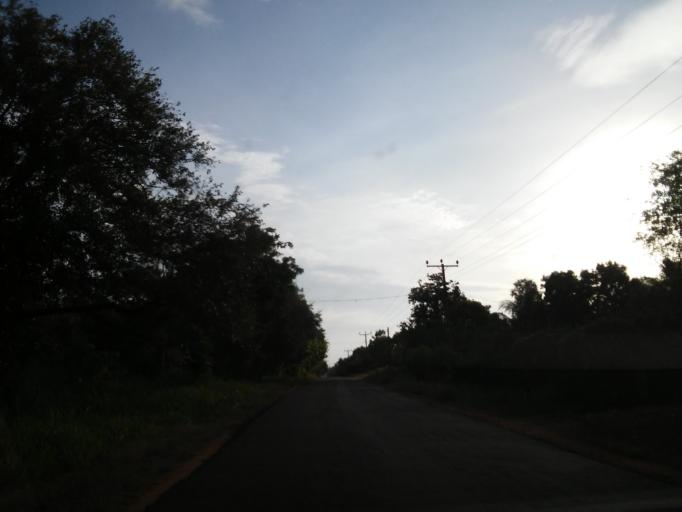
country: LK
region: Central
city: Sigiriya
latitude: 8.1592
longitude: 80.6533
